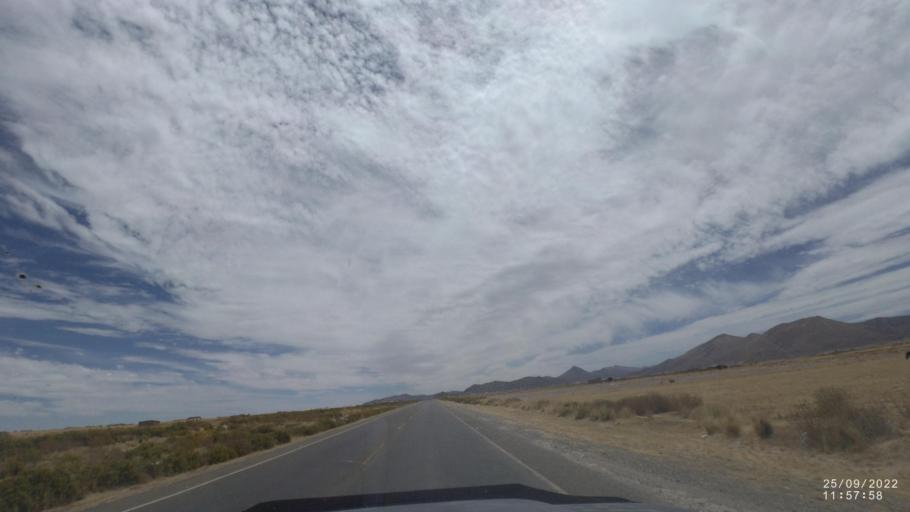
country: BO
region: Oruro
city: Challapata
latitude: -18.8136
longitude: -66.8328
